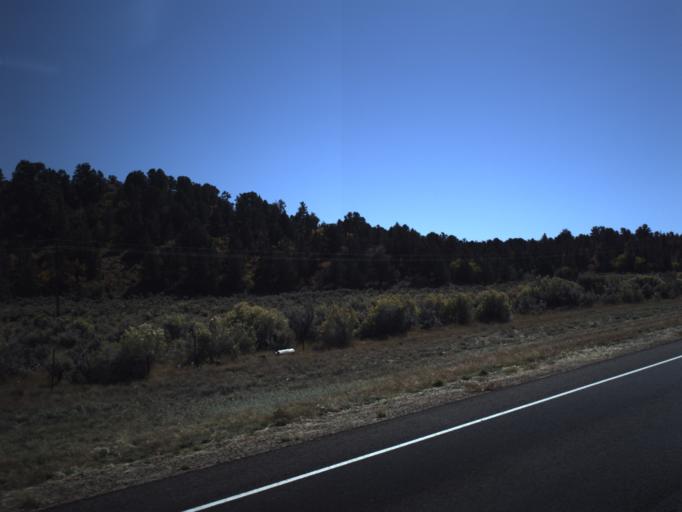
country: US
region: Utah
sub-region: Garfield County
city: Panguitch
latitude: 37.6517
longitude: -111.8415
